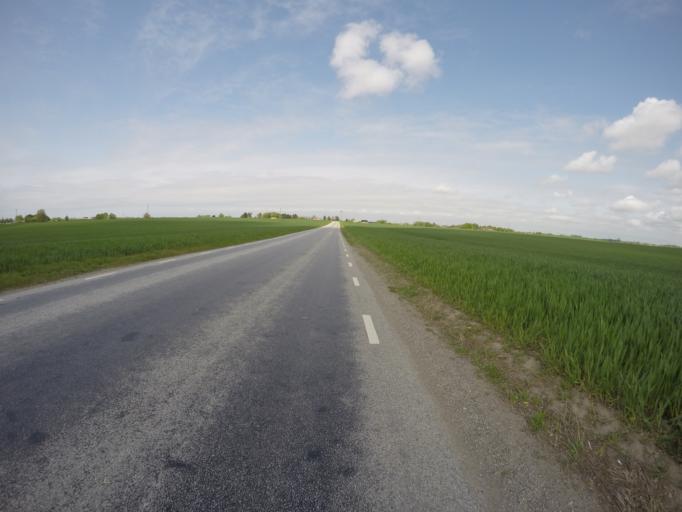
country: SE
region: Skane
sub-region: Malmo
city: Tygelsjo
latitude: 55.5360
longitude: 13.0306
